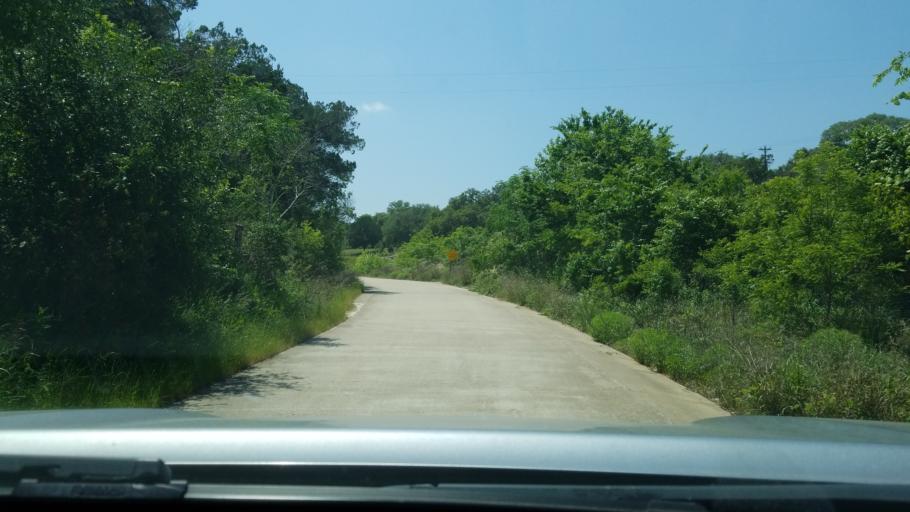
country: US
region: Texas
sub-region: Blanco County
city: Blanco
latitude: 30.0015
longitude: -98.4131
